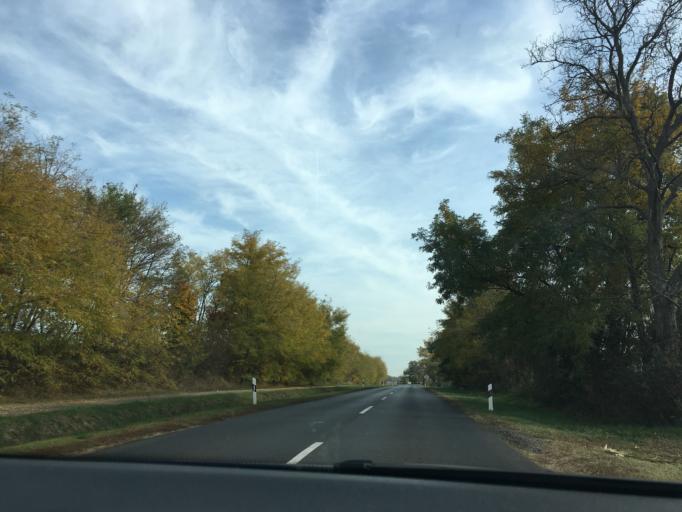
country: HU
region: Szabolcs-Szatmar-Bereg
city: Kallosemjen
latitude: 47.8617
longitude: 21.8916
